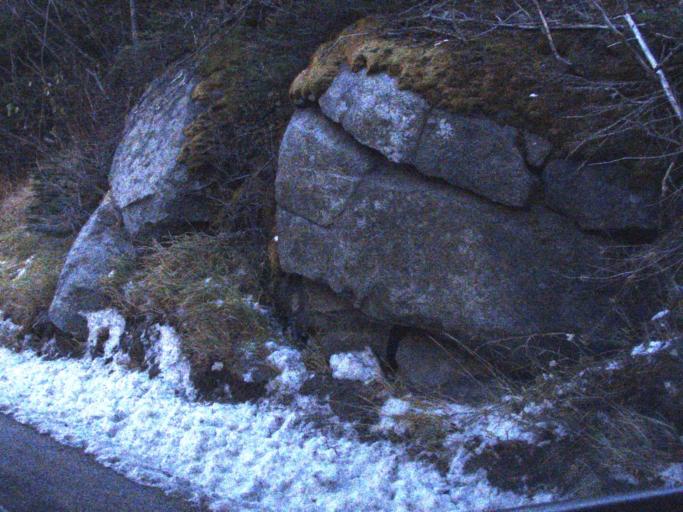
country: US
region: Washington
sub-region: Ferry County
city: Republic
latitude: 48.6044
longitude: -118.4969
